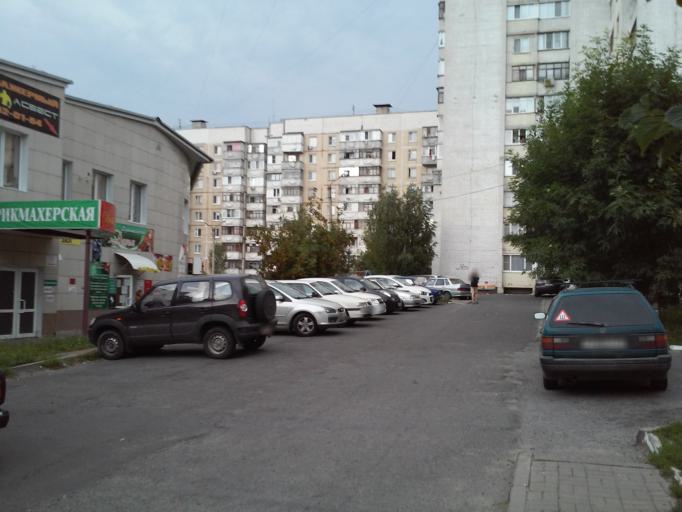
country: RU
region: Belgorod
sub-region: Belgorodskiy Rayon
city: Belgorod
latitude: 50.5685
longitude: 36.5767
